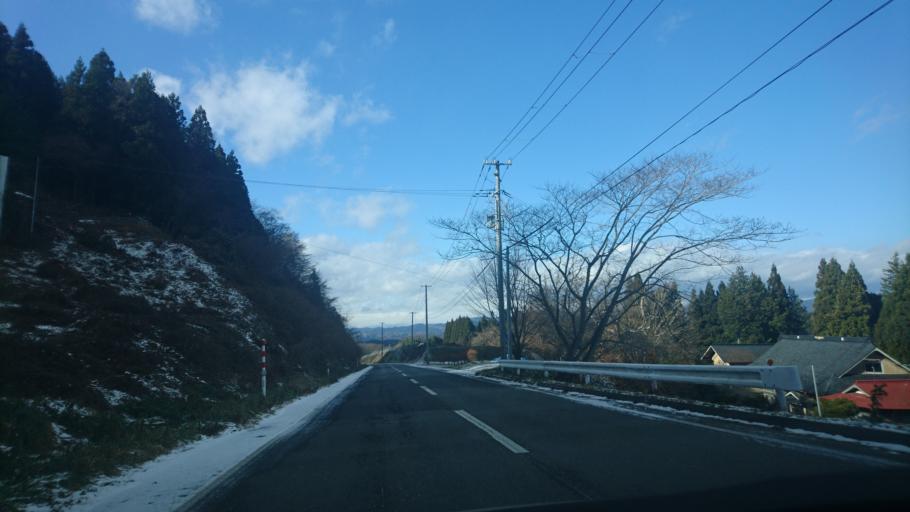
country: JP
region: Iwate
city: Ichinoseki
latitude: 38.9739
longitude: 141.3938
